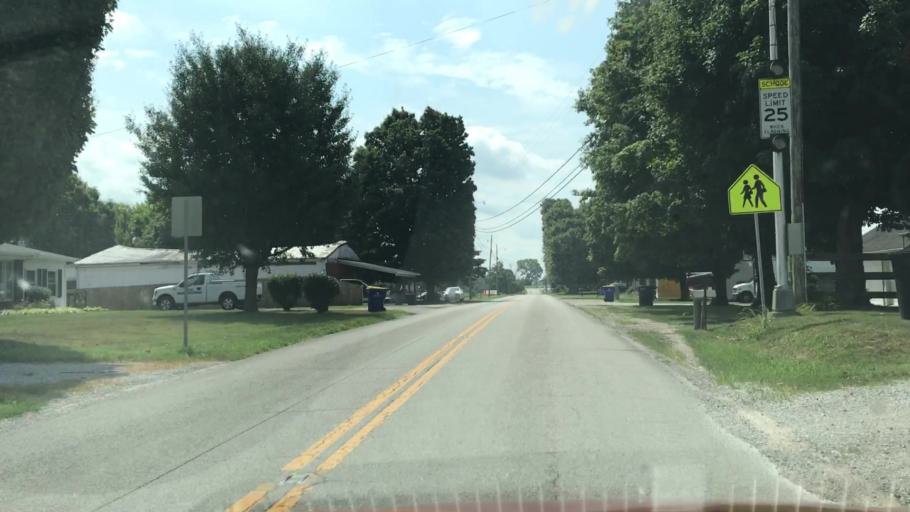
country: US
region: Kentucky
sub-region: Barren County
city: Glasgow
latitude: 36.8877
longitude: -85.8488
